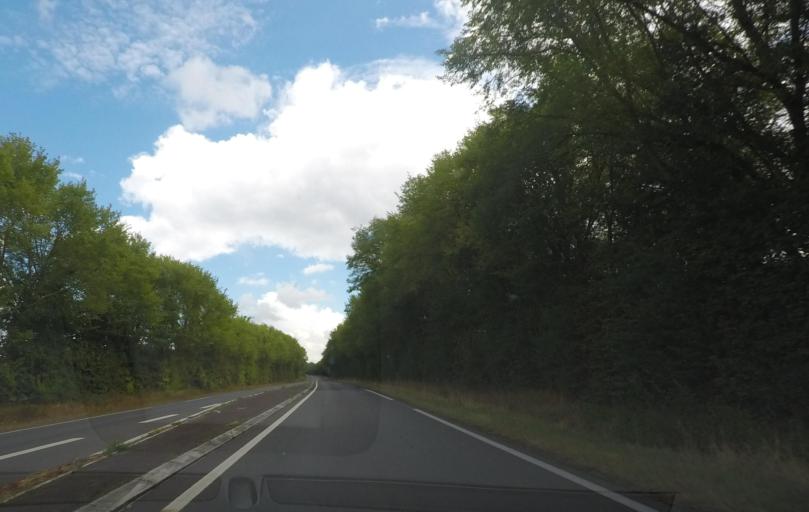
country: FR
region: Pays de la Loire
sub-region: Departement de la Sarthe
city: Champagne
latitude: 48.0727
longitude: 0.3020
